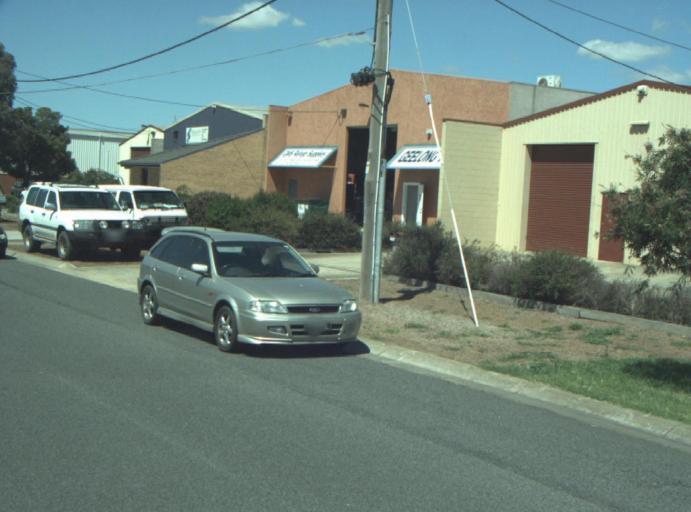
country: AU
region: Victoria
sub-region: Greater Geelong
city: Breakwater
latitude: -38.1945
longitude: 144.3481
